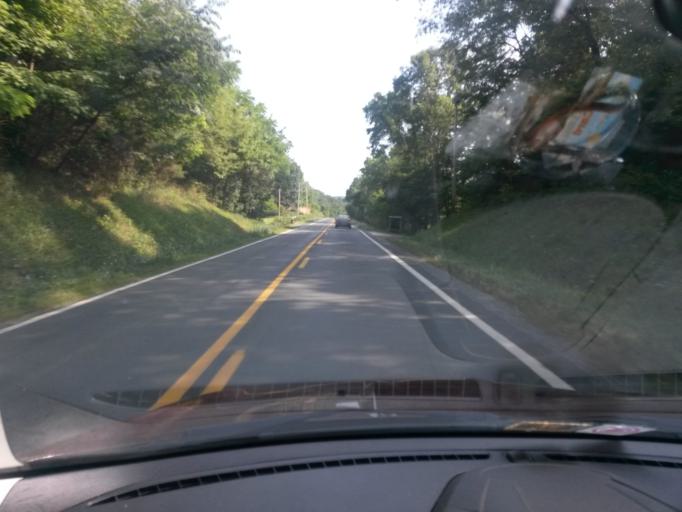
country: US
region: Virginia
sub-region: Shenandoah County
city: Basye
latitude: 38.9003
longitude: -78.8519
